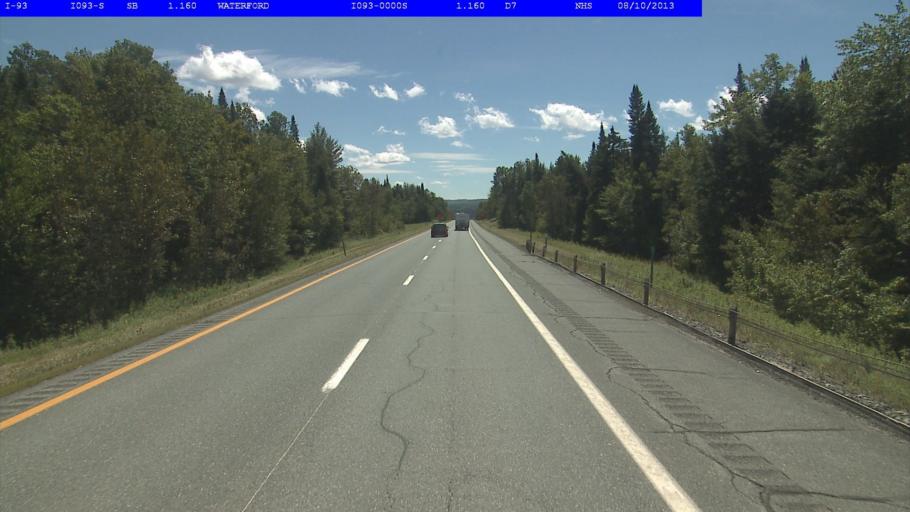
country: US
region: Vermont
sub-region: Caledonia County
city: Saint Johnsbury
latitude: 44.3592
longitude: -71.8987
